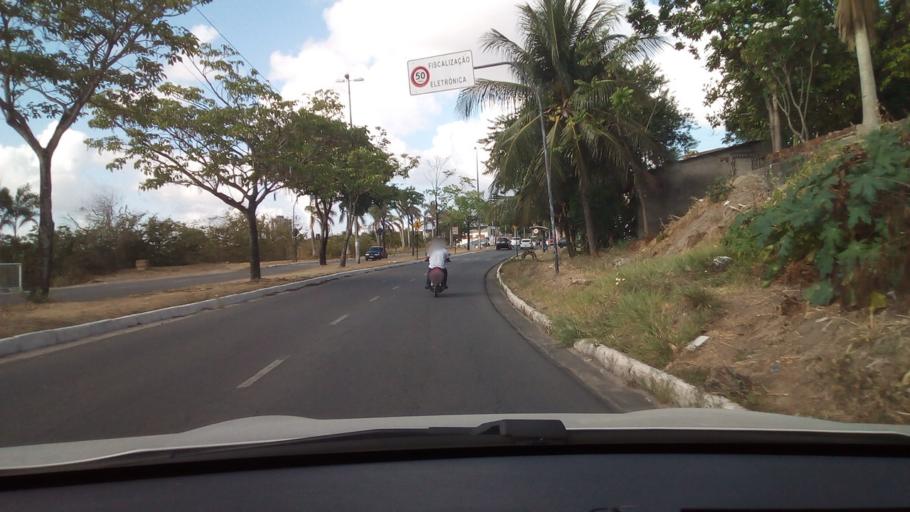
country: BR
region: Paraiba
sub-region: Joao Pessoa
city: Joao Pessoa
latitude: -7.1267
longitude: -34.8505
